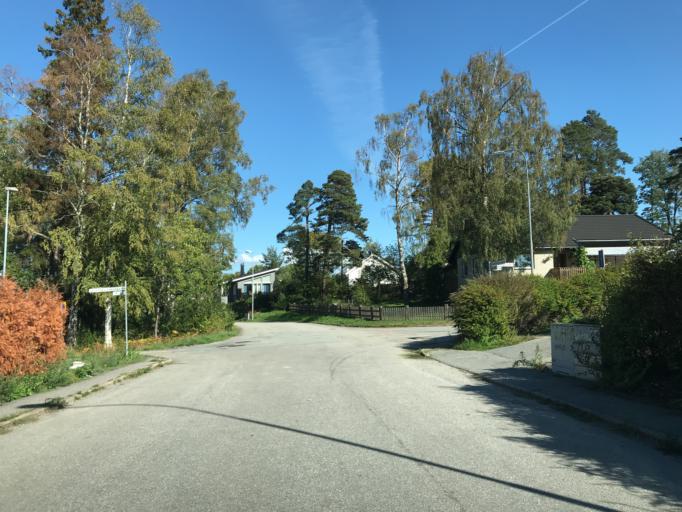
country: SE
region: Stockholm
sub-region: Sollentuna Kommun
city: Sollentuna
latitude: 59.4214
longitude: 17.9510
